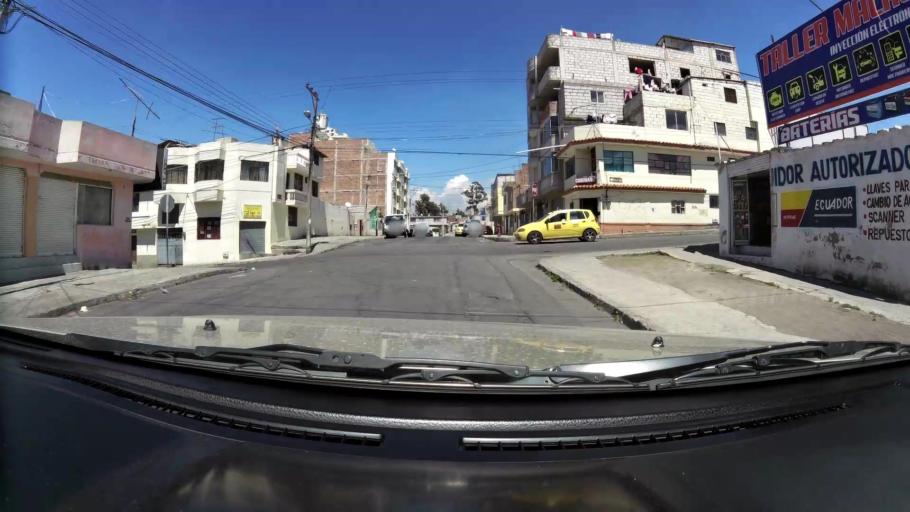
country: EC
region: Chimborazo
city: Riobamba
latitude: -1.6625
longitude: -78.6480
